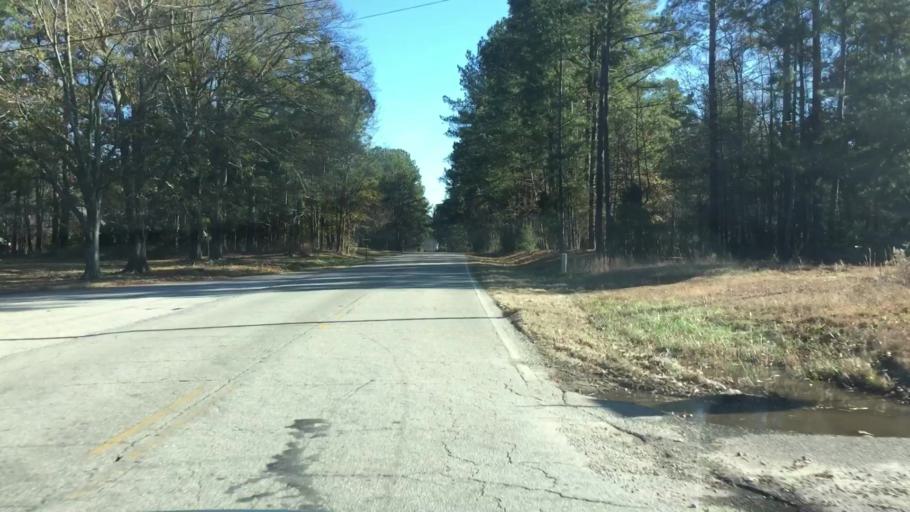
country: US
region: Georgia
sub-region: Newton County
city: Oakwood
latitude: 33.4710
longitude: -84.0161
